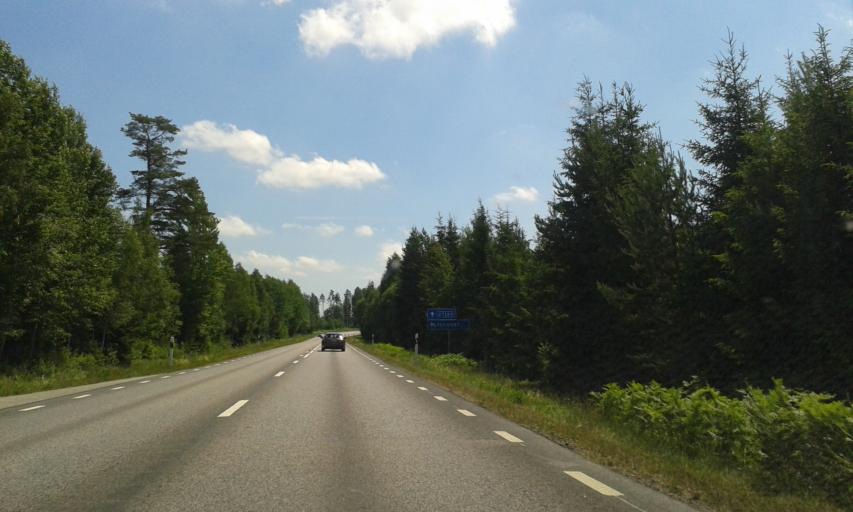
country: SE
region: Kronoberg
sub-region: Vaxjo Kommun
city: Ingelstad
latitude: 56.7812
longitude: 14.9049
